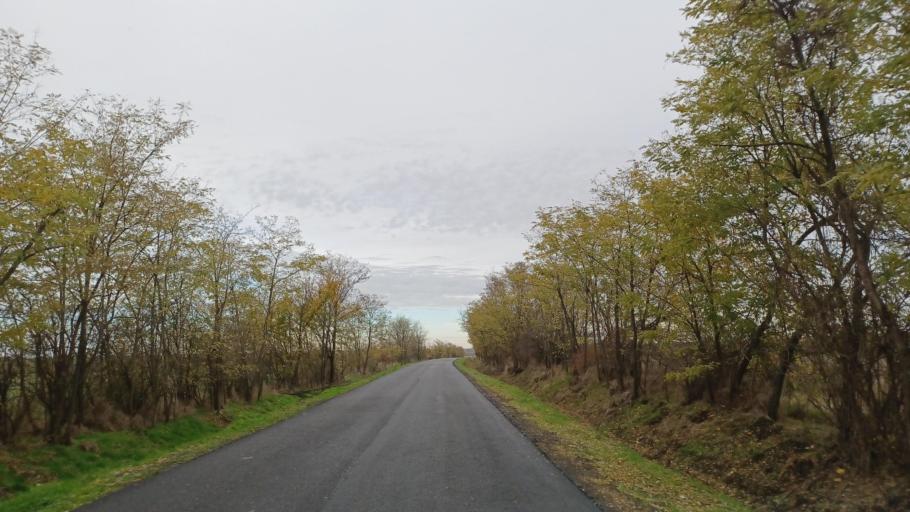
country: HU
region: Tolna
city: Tengelic
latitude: 46.5449
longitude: 18.7534
